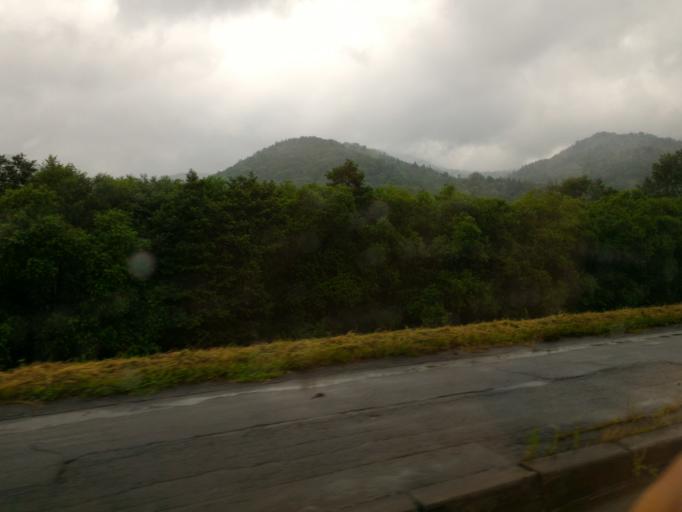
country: JP
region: Hokkaido
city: Nayoro
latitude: 44.7325
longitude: 142.1977
